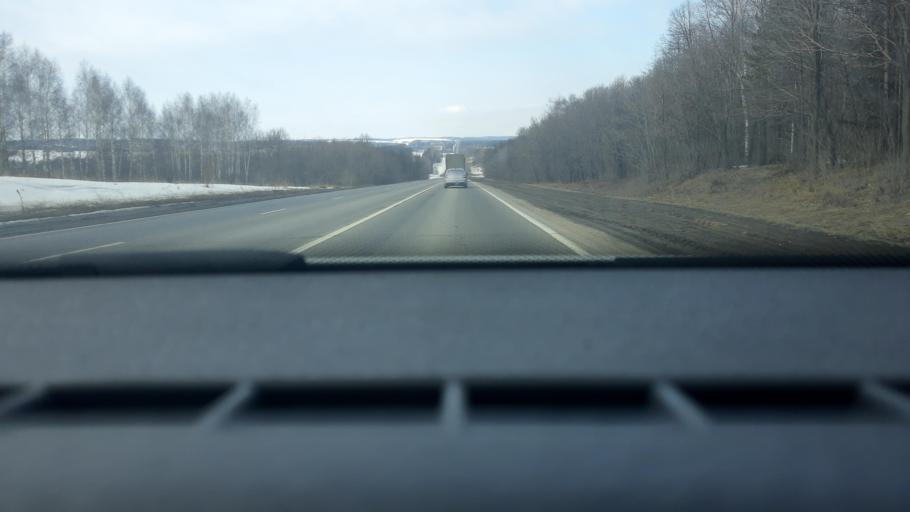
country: RU
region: Bashkortostan
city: Iglino
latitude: 54.7950
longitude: 56.5839
